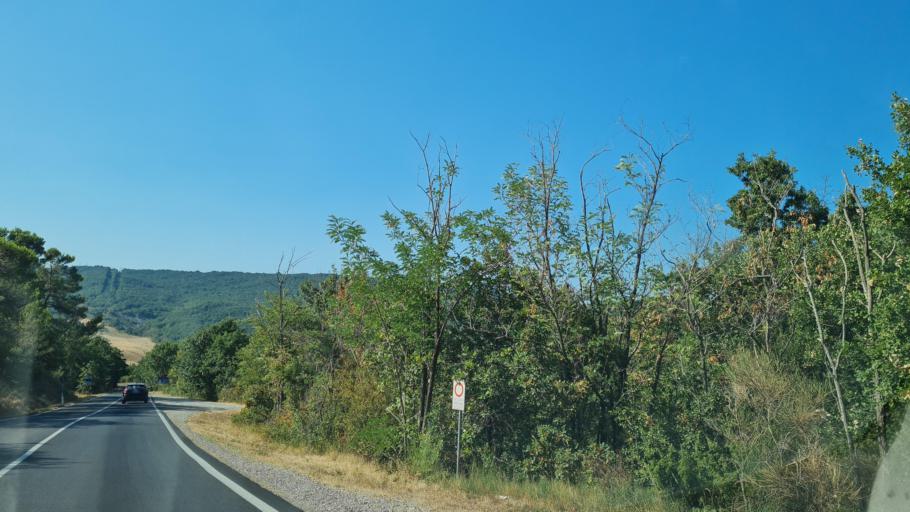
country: IT
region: Tuscany
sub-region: Provincia di Siena
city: Chianciano Terme
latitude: 43.0375
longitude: 11.7980
